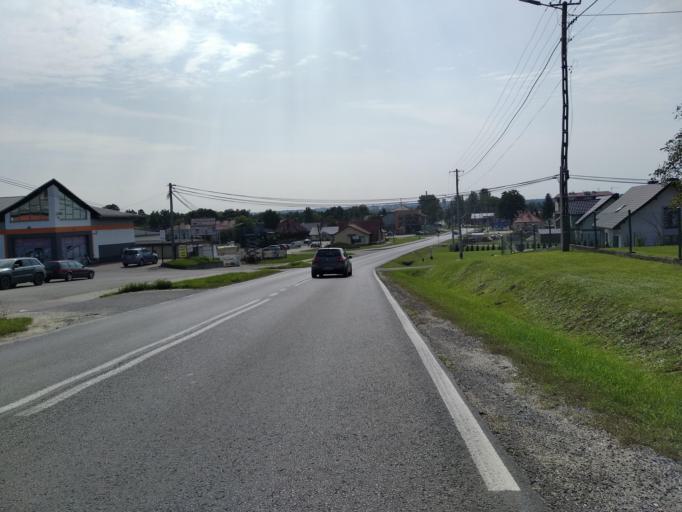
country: PL
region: Subcarpathian Voivodeship
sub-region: Powiat ropczycko-sedziszowski
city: Ostrow
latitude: 50.1011
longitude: 21.5932
